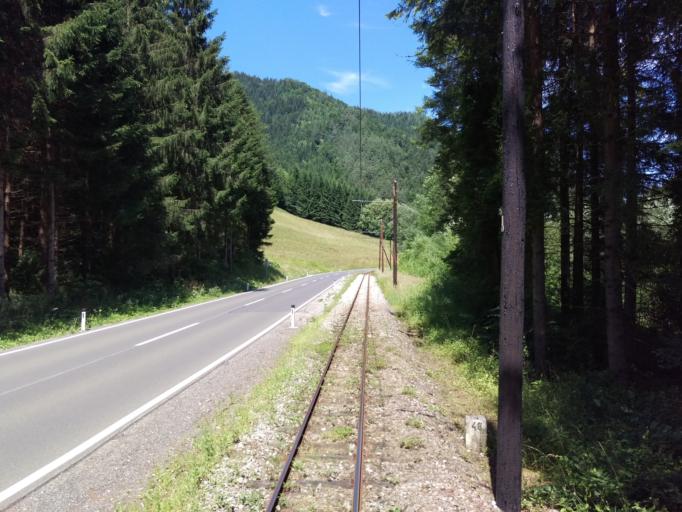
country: AT
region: Styria
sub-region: Politischer Bezirk Bruck-Muerzzuschlag
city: Pernegg an der Mur
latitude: 47.3653
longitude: 15.3797
